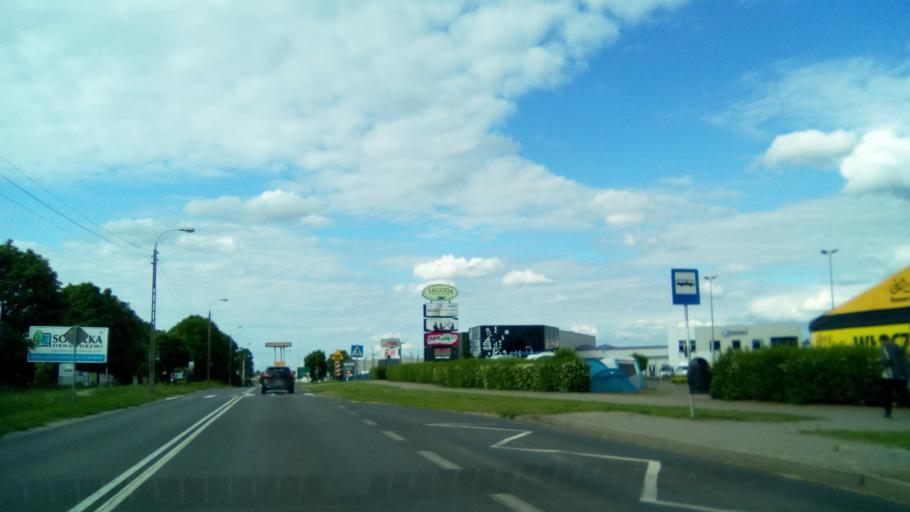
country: PL
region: Greater Poland Voivodeship
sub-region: Powiat gnieznienski
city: Gniezno
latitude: 52.5592
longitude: 17.6084
